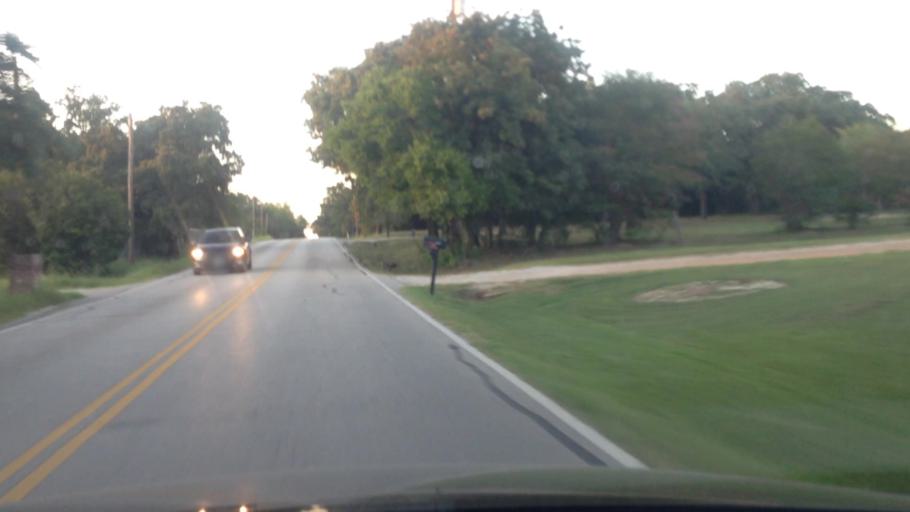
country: US
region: Texas
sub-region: Tarrant County
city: Keller
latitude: 32.9426
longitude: -97.2031
